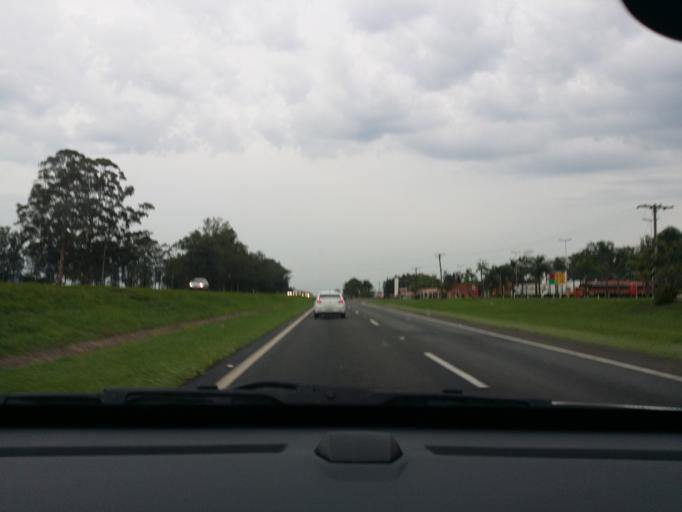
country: BR
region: Sao Paulo
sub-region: Sao Carlos
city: Sao Carlos
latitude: -22.0908
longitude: -47.8325
